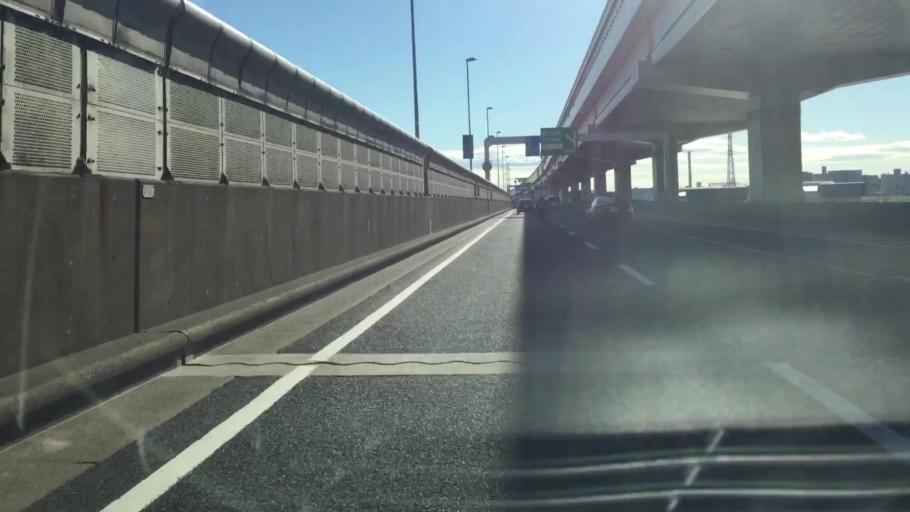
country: JP
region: Saitama
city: Soka
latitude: 35.7435
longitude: 139.8243
